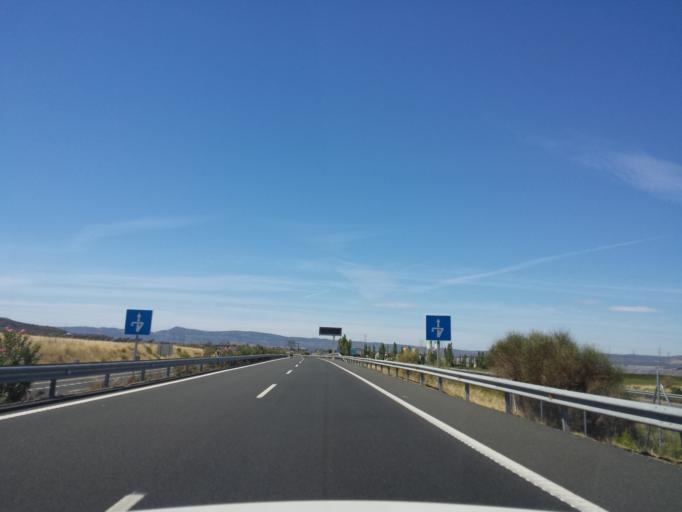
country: ES
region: Extremadura
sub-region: Provincia de Caceres
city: Saucedilla
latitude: 39.8341
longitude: -5.6525
